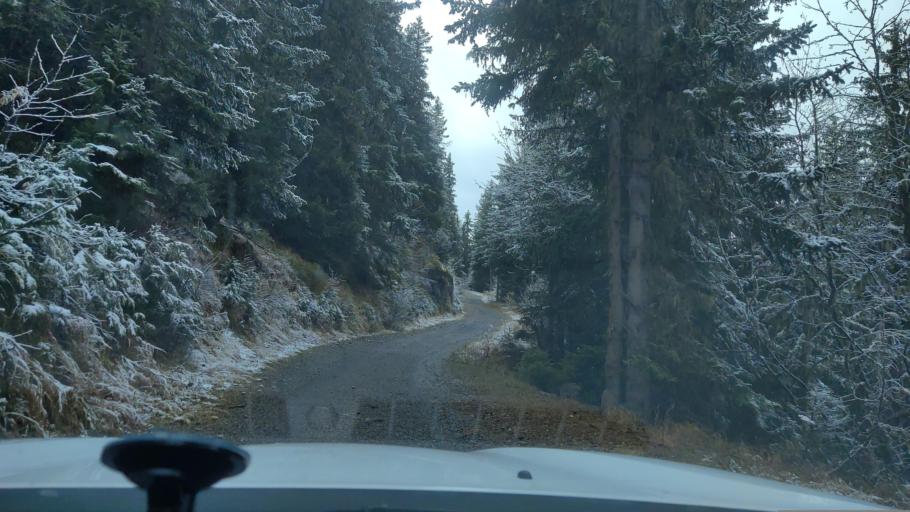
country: FR
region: Rhone-Alpes
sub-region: Departement de la Savoie
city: Seez
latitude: 45.5983
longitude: 6.8089
